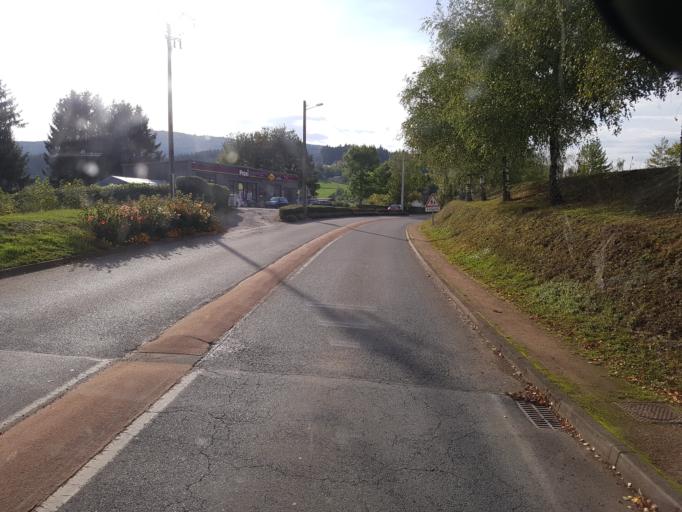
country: FR
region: Rhone-Alpes
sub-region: Departement de la Loire
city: Belmont-de-la-Loire
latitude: 46.1952
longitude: 4.4372
